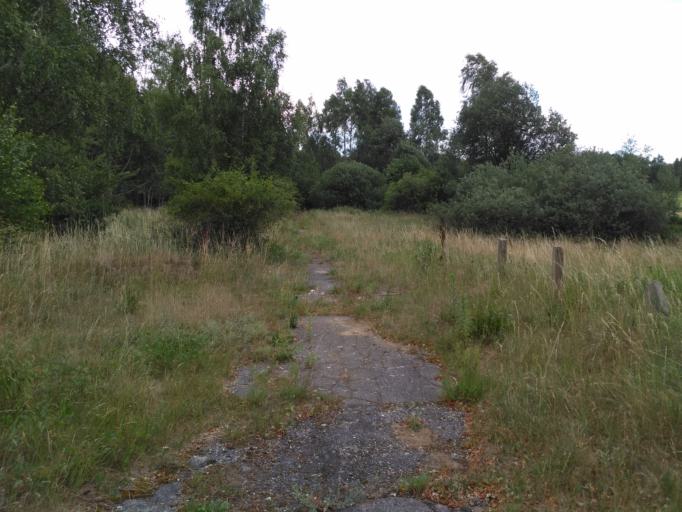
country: DE
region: Saxony
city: Tauscha
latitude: 51.2994
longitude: 13.8362
